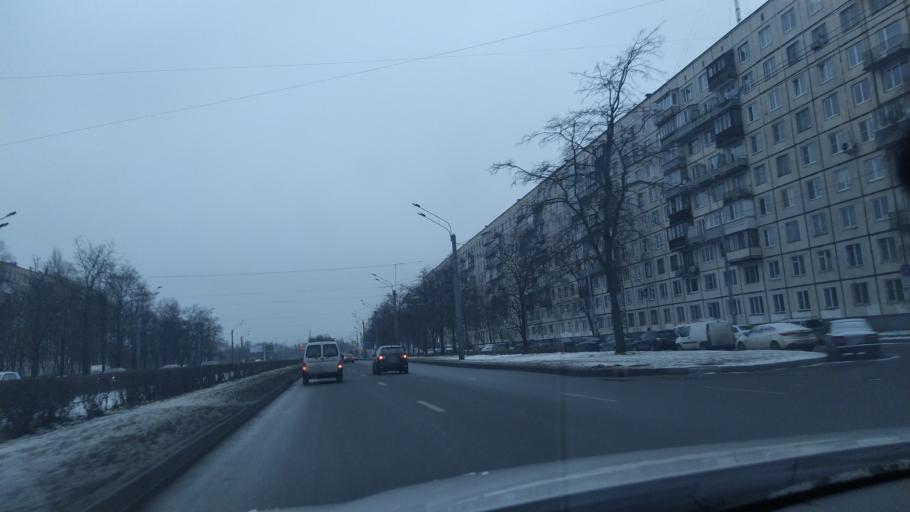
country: RU
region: St.-Petersburg
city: Grazhdanka
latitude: 60.0336
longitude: 30.3936
